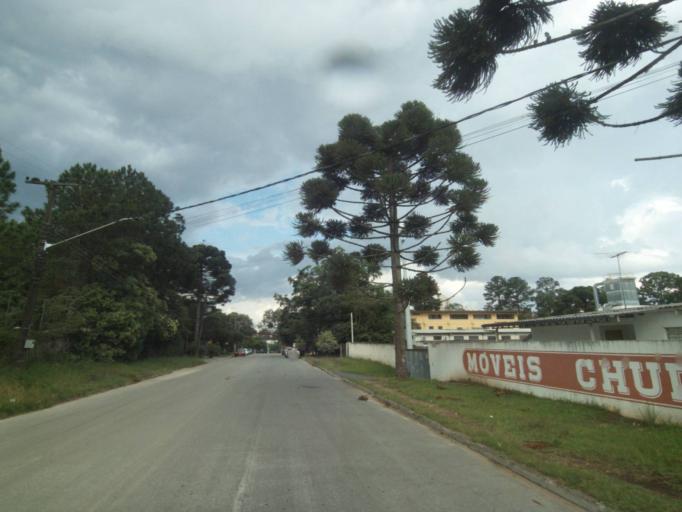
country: BR
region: Parana
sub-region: Curitiba
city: Curitiba
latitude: -25.4486
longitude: -49.3617
